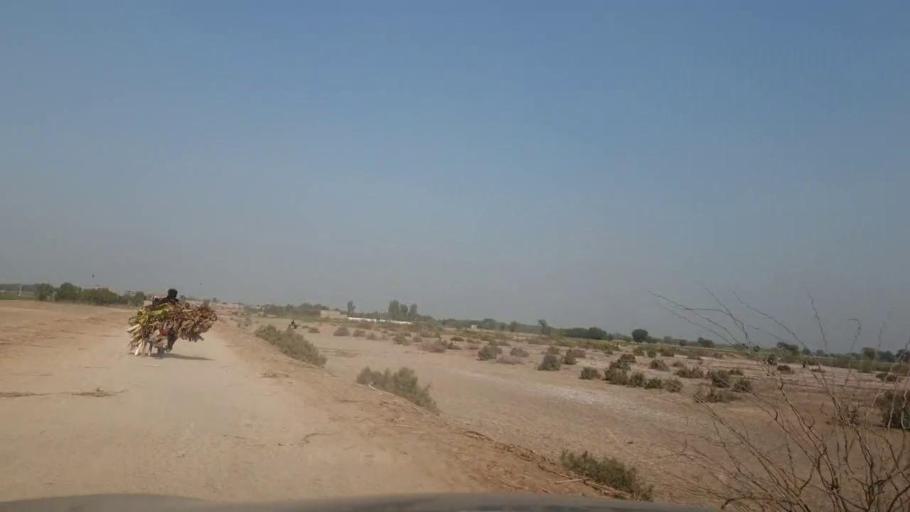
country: PK
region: Sindh
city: Tando Allahyar
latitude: 25.5458
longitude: 68.7120
